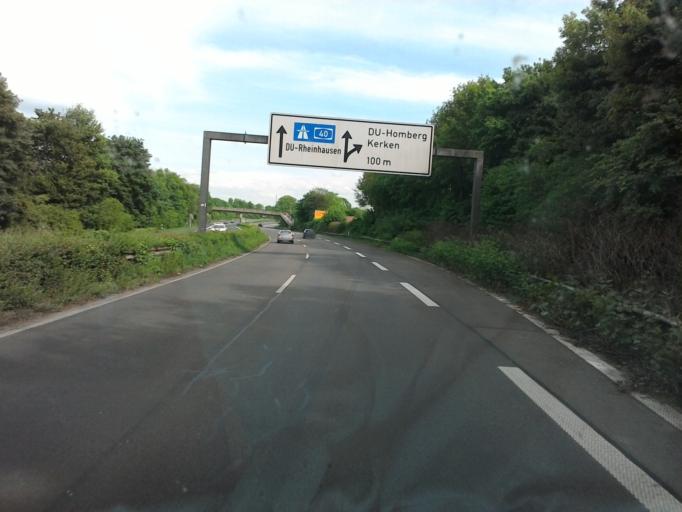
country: DE
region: North Rhine-Westphalia
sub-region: Regierungsbezirk Dusseldorf
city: Moers
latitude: 51.4417
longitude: 6.6636
